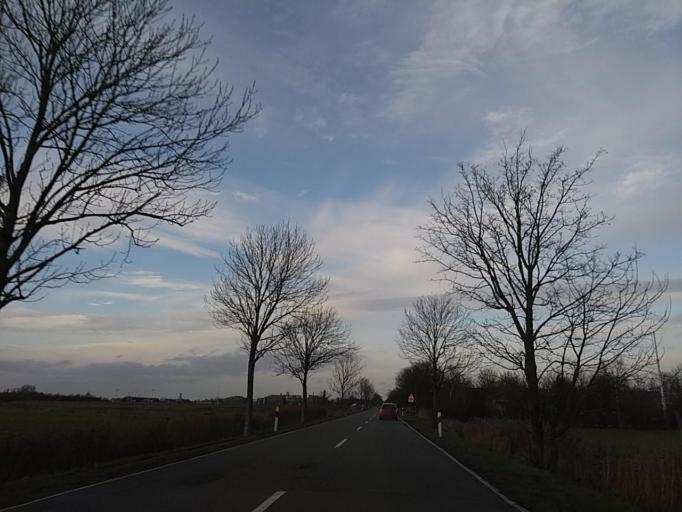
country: DE
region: Lower Saxony
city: Jemgum
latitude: 53.2424
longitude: 7.3915
